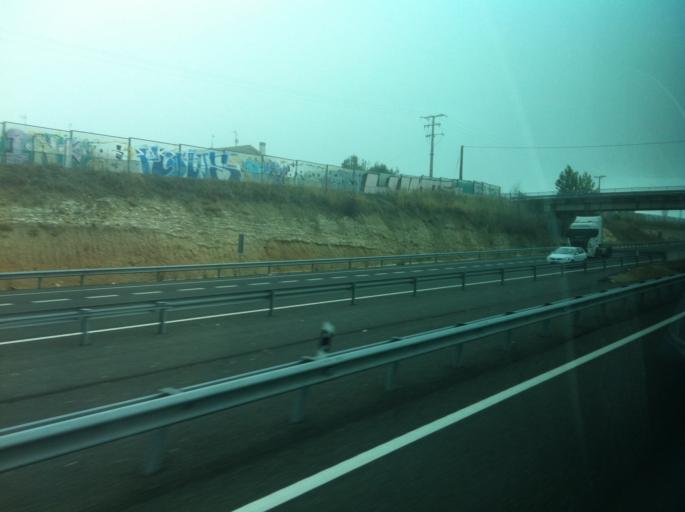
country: ES
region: Castille and Leon
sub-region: Provincia de Burgos
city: Saldana de Burgos
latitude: 42.2595
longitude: -3.6994
